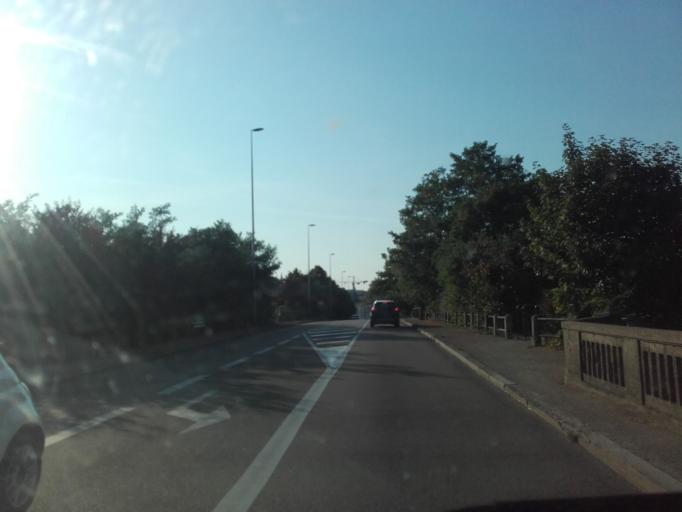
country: FR
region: Bourgogne
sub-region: Departement de l'Yonne
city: Auxerre
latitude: 47.7945
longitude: 3.5852
